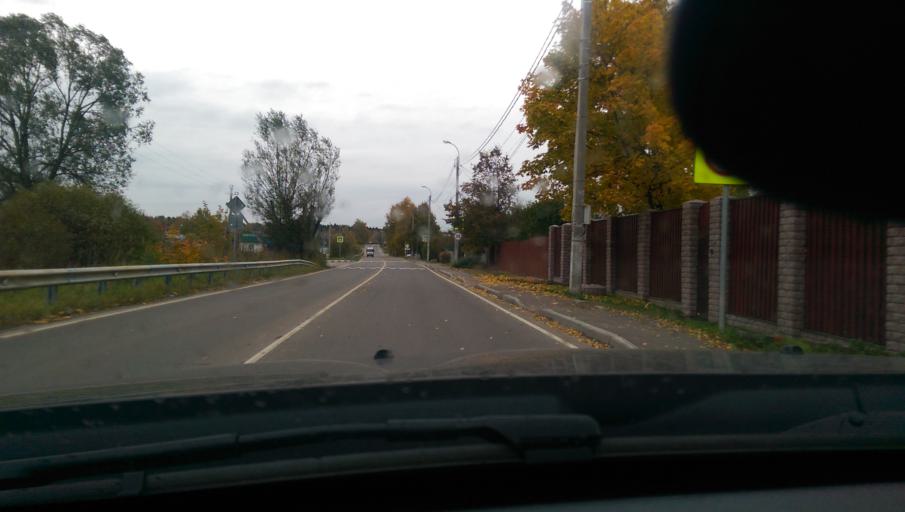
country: RU
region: Moskovskaya
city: Pirogovskiy
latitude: 56.0121
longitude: 37.7175
